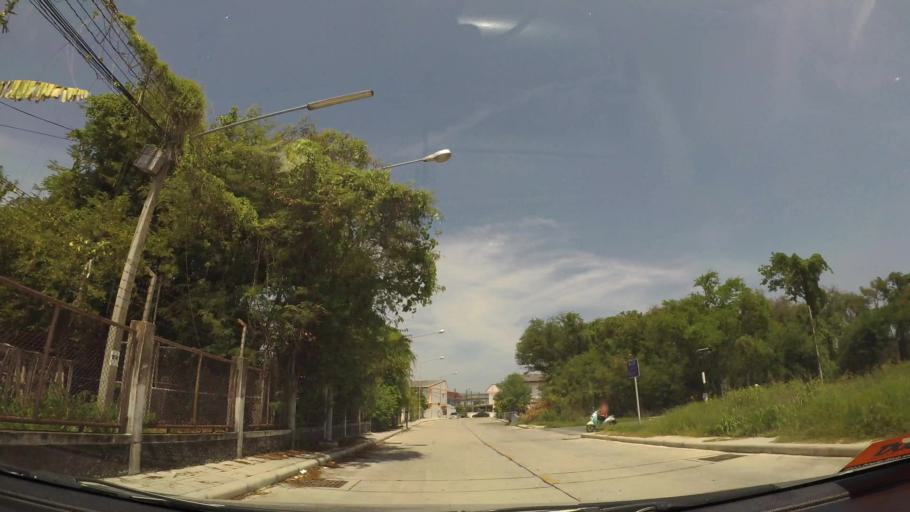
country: TH
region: Chon Buri
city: Chon Buri
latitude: 13.3280
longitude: 100.9493
